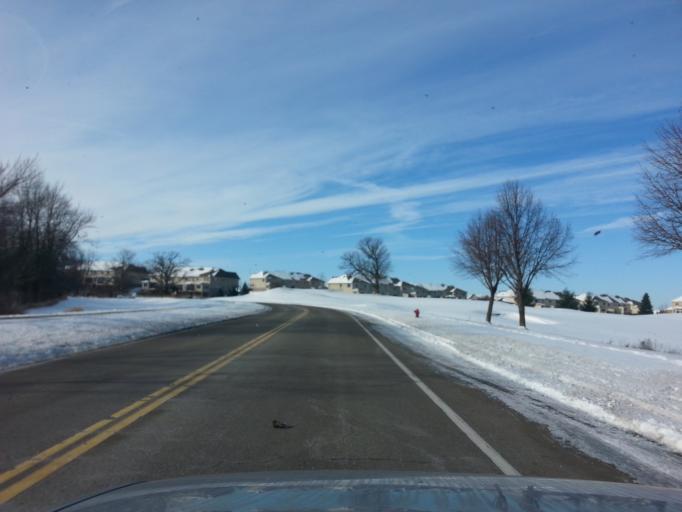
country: US
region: Minnesota
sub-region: Scott County
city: Prior Lake
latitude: 44.7414
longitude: -93.4653
